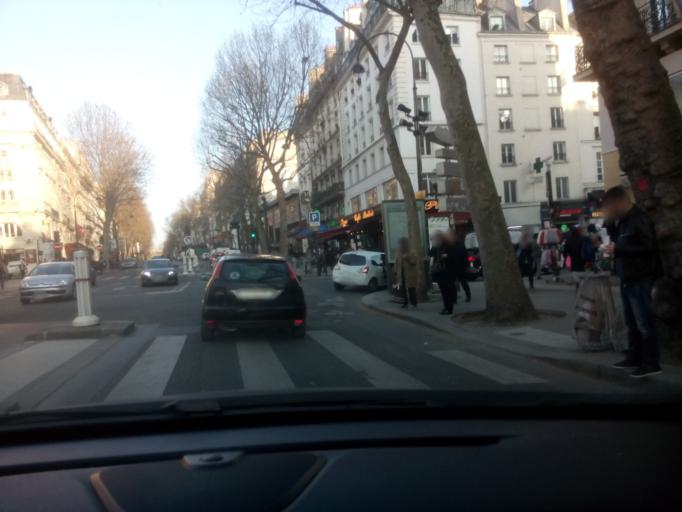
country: FR
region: Ile-de-France
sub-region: Paris
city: Paris
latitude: 48.8697
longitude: 2.3551
